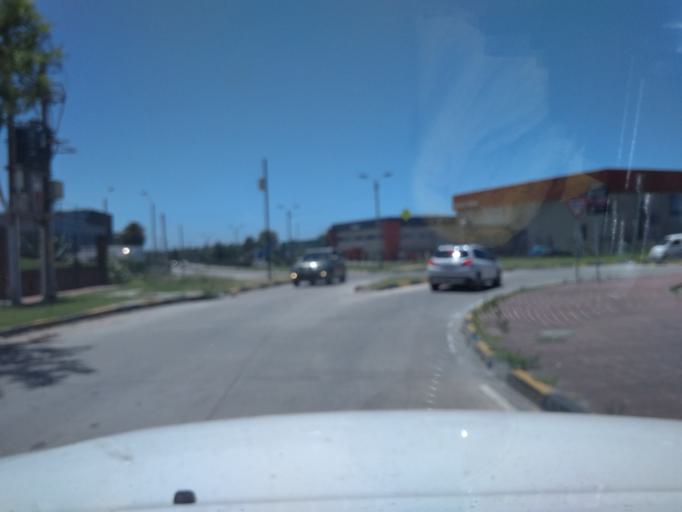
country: UY
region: Canelones
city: Paso de Carrasco
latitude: -34.8798
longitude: -56.0808
